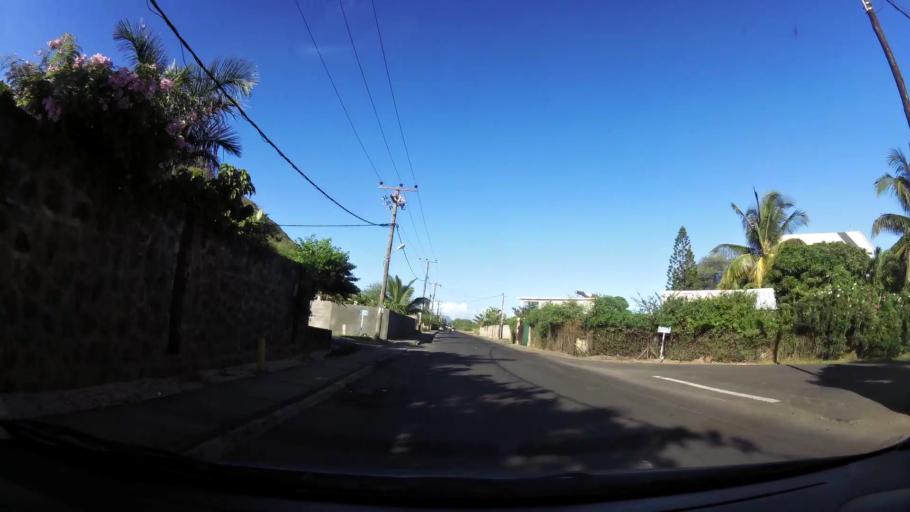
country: MU
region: Black River
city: Tamarin
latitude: -20.3339
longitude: 57.3717
